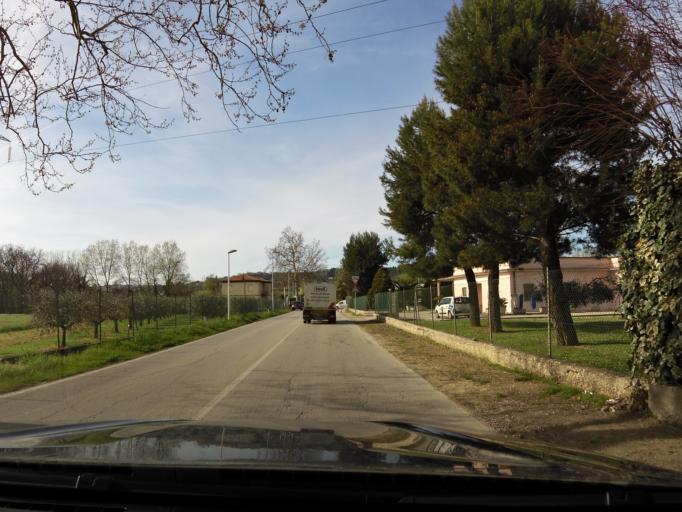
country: IT
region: The Marches
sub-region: Provincia di Ancona
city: Villa Musone
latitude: 43.4539
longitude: 13.5970
